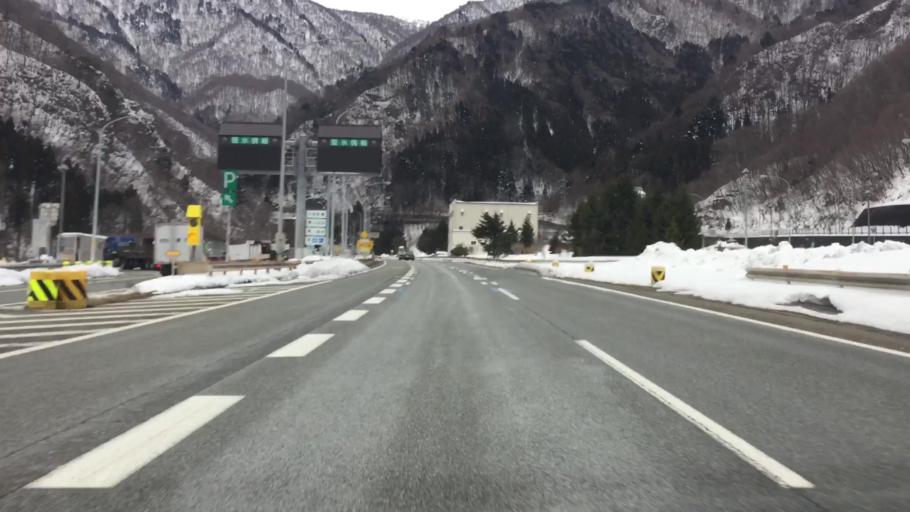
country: JP
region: Gunma
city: Numata
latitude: 36.7774
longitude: 138.9443
